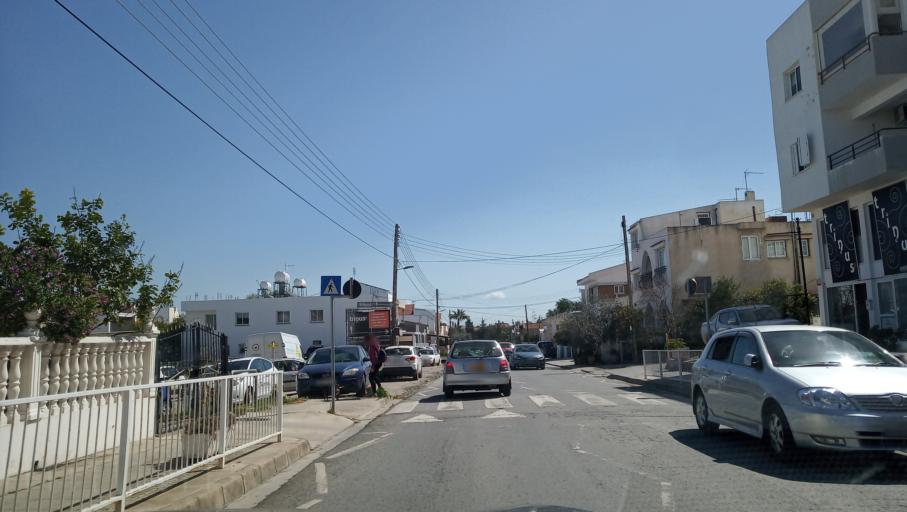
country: CY
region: Lefkosia
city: Kato Deftera
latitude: 35.1225
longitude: 33.2981
